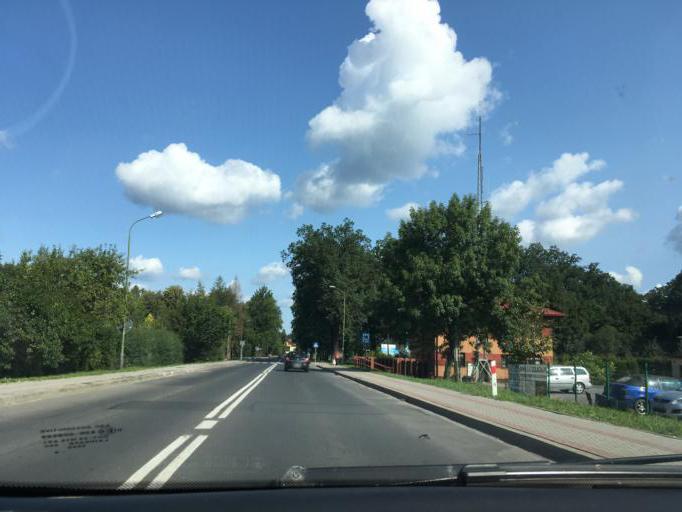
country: PL
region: Subcarpathian Voivodeship
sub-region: Powiat leski
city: Lesko
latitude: 49.4767
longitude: 22.3245
